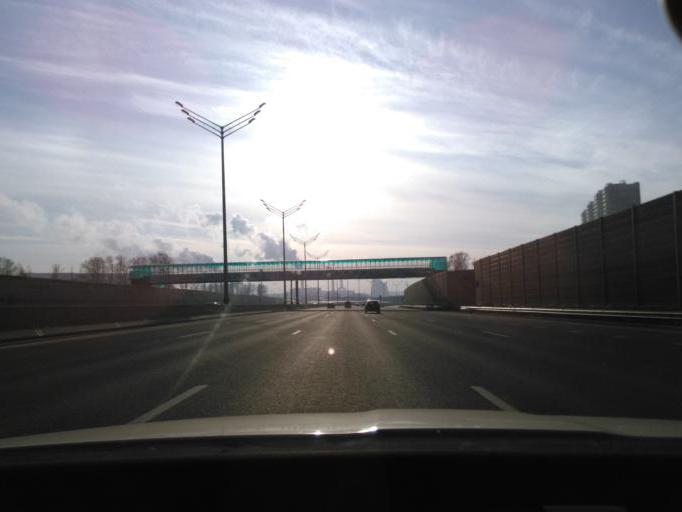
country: RU
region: Moskovskaya
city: Levoberezhnaya
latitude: 55.9050
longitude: 37.4794
